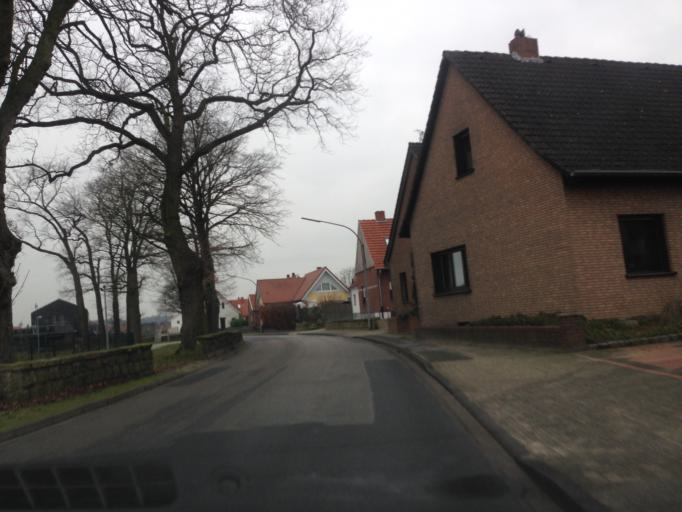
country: DE
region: Lower Saxony
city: Bad Bentheim
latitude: 52.2980
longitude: 7.1679
